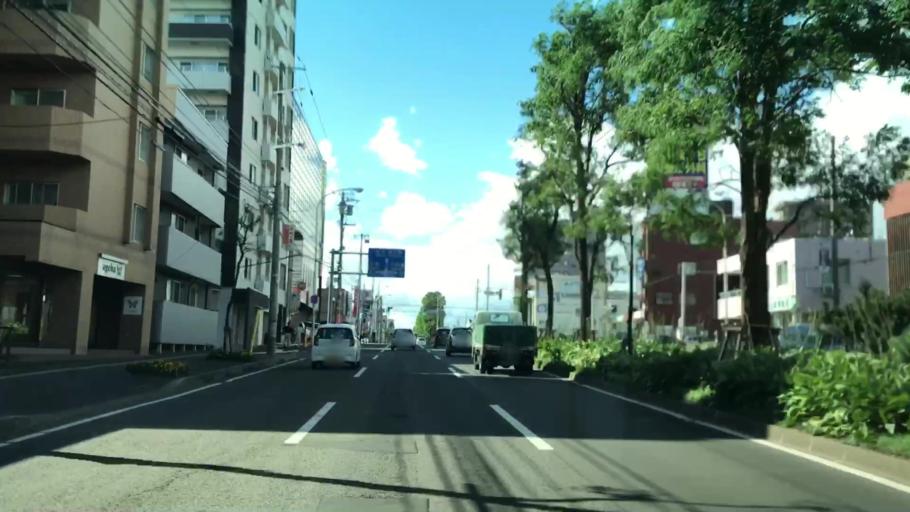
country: JP
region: Hokkaido
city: Sapporo
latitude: 43.0353
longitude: 141.4240
